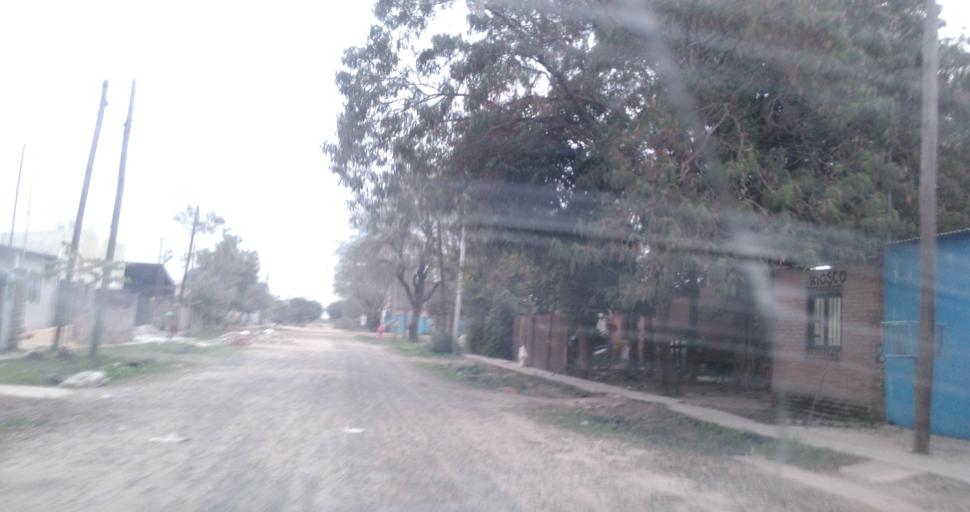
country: AR
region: Chaco
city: Fontana
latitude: -27.4493
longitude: -59.0368
